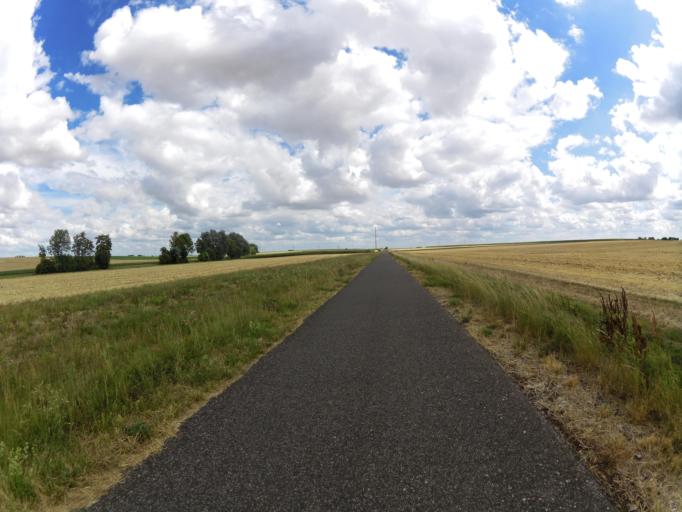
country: DE
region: Bavaria
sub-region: Regierungsbezirk Unterfranken
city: Aub
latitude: 49.5675
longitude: 10.0315
